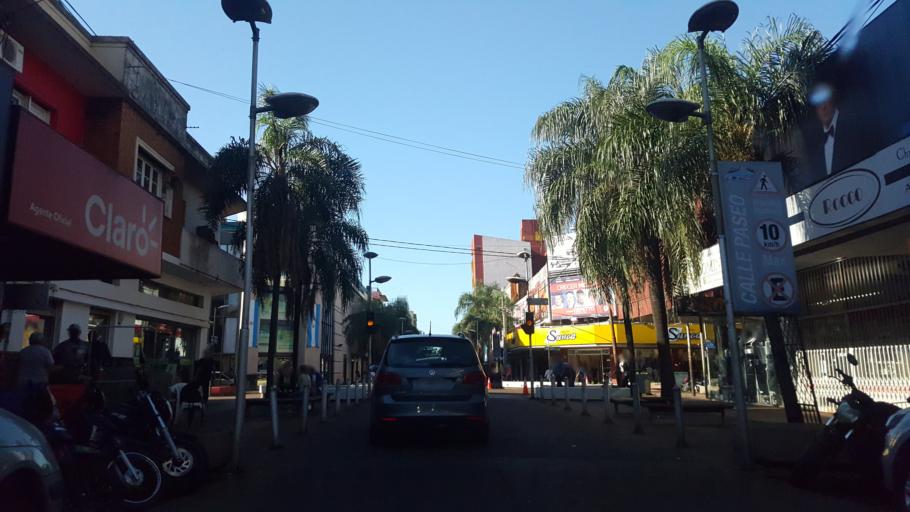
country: AR
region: Misiones
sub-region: Departamento de Capital
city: Posadas
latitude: -27.3663
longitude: -55.8957
